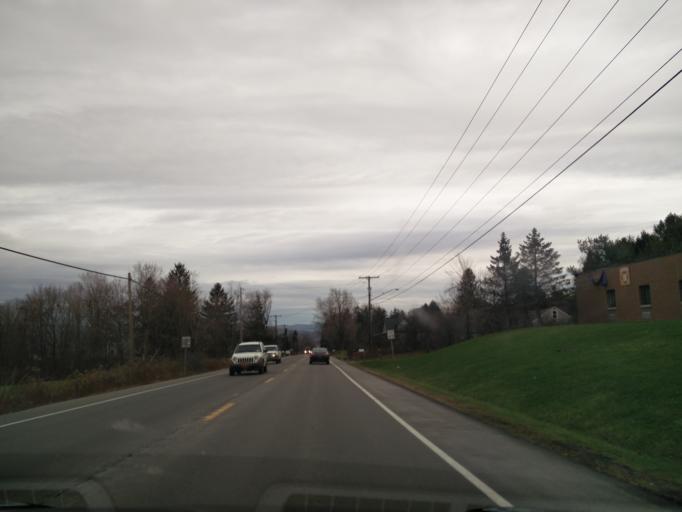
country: US
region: New York
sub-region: Tompkins County
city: Northwest Ithaca
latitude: 42.4638
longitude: -76.5352
